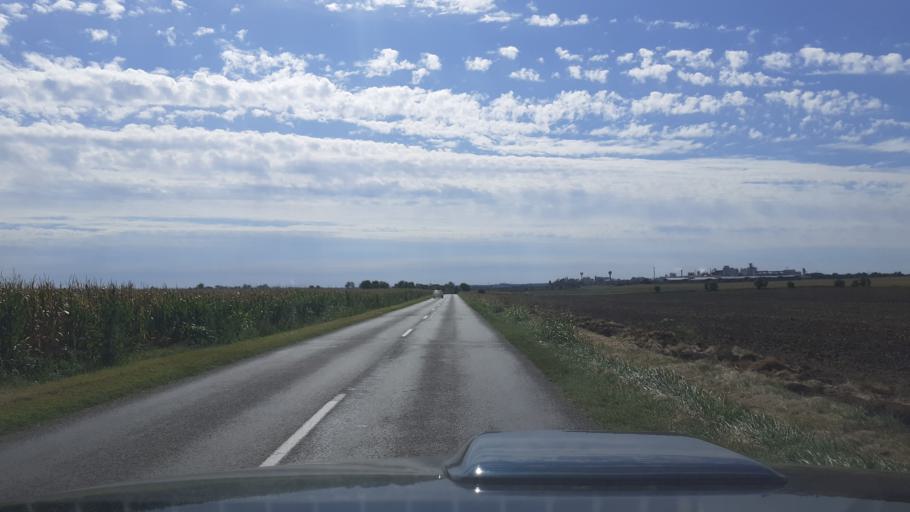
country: HU
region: Fejer
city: Pusztaszabolcs
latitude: 47.1035
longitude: 18.7105
